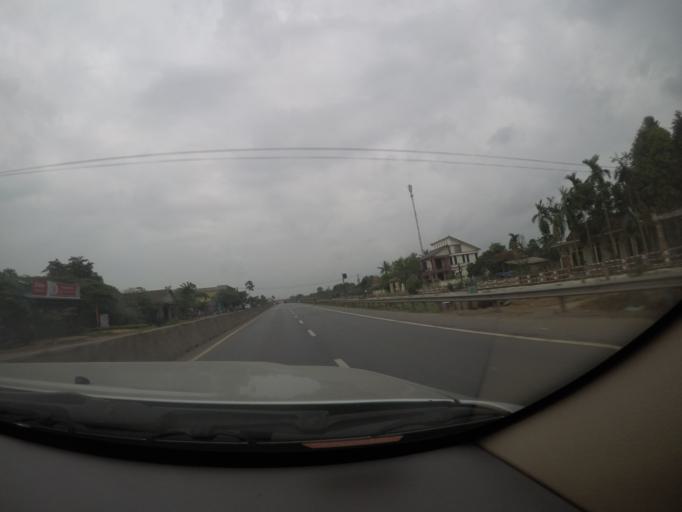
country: VN
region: Quang Tri
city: Hai Lang
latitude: 16.6386
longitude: 107.2970
